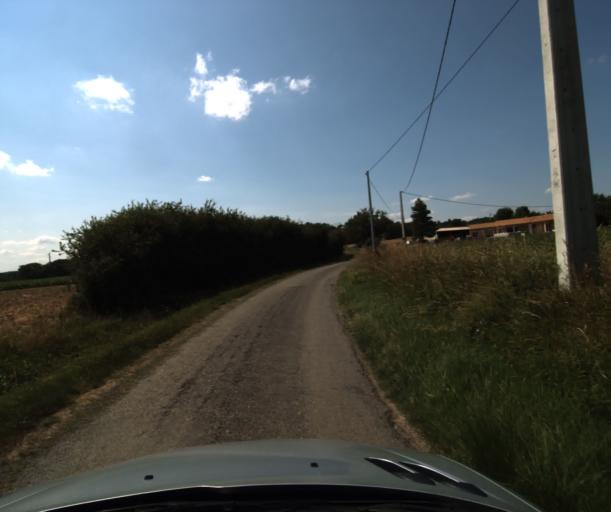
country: FR
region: Midi-Pyrenees
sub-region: Departement de la Haute-Garonne
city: Saint-Lys
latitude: 43.5290
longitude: 1.1583
